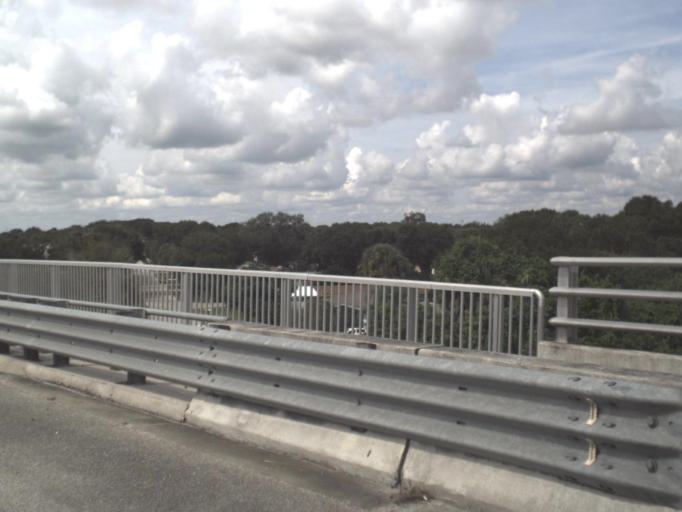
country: US
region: Florida
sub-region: Okeechobee County
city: Cypress Quarters
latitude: 27.2447
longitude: -80.8078
